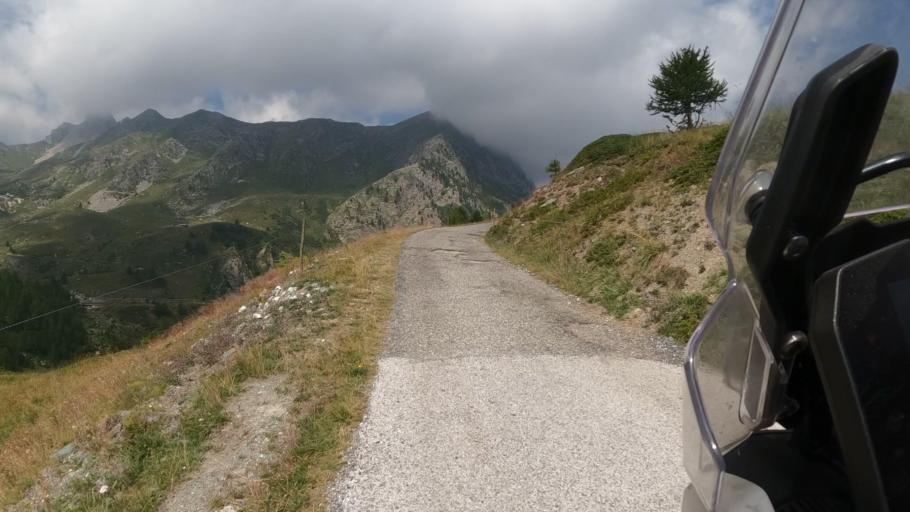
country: IT
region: Piedmont
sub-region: Provincia di Cuneo
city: Marmora
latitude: 44.4009
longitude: 7.1136
